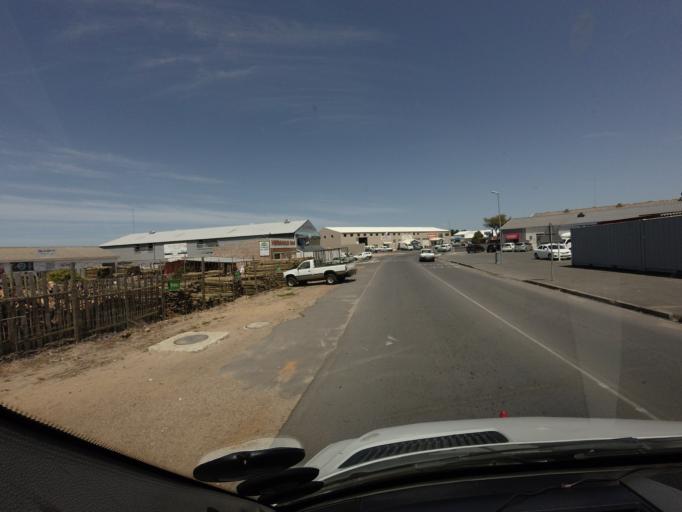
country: ZA
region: Western Cape
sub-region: Overberg District Municipality
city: Hermanus
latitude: -34.4211
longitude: 19.2246
